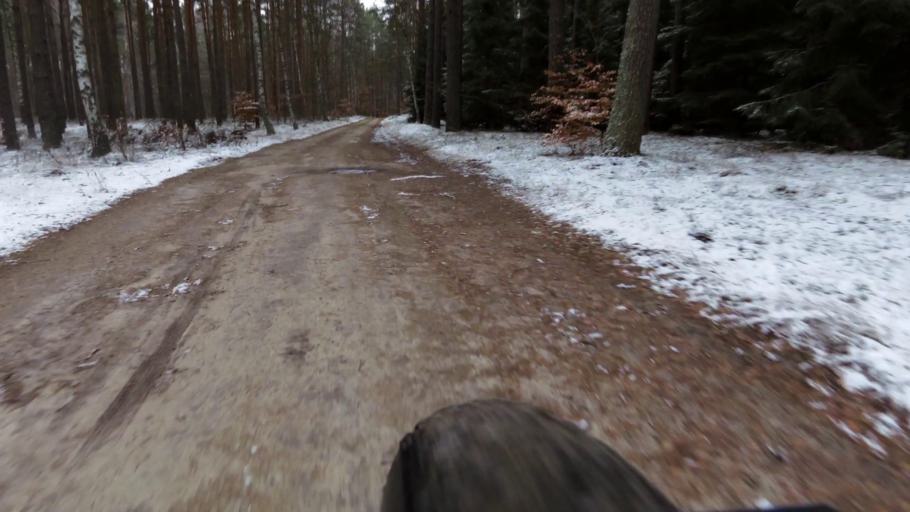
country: PL
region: West Pomeranian Voivodeship
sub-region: Powiat walecki
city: Miroslawiec
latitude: 53.3091
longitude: 16.0679
